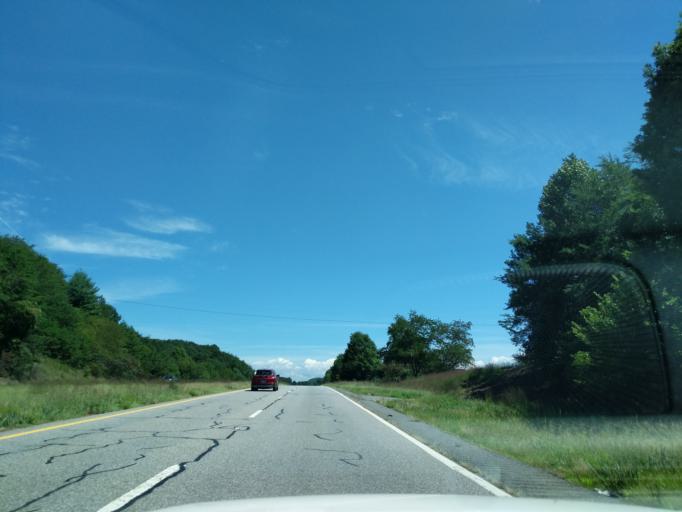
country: US
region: Georgia
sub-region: Fannin County
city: Blue Ridge
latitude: 34.8902
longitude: -84.2322
